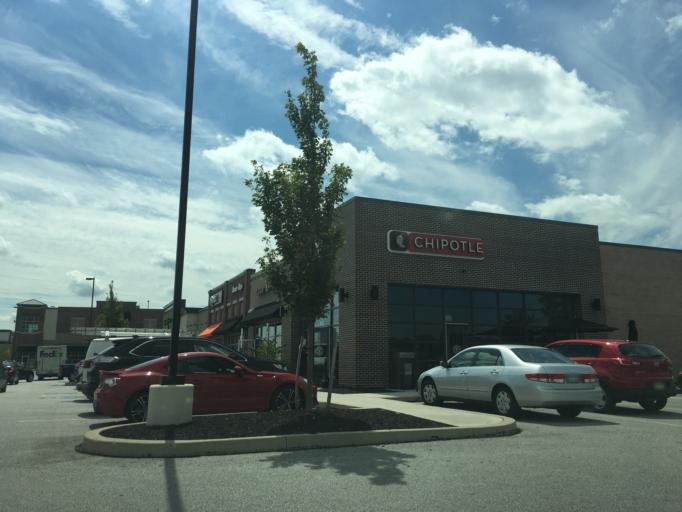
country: US
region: Pennsylvania
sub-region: York County
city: Shrewsbury
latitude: 39.7700
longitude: -76.6722
